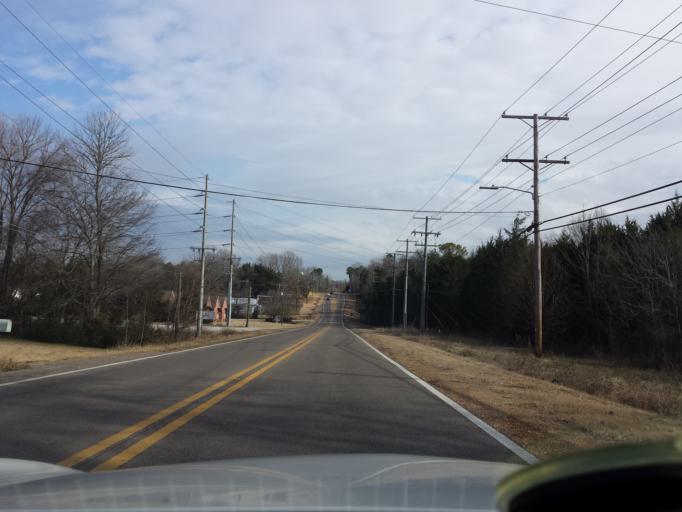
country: US
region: Mississippi
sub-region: Oktibbeha County
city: Starkville
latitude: 33.4628
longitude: -88.8367
